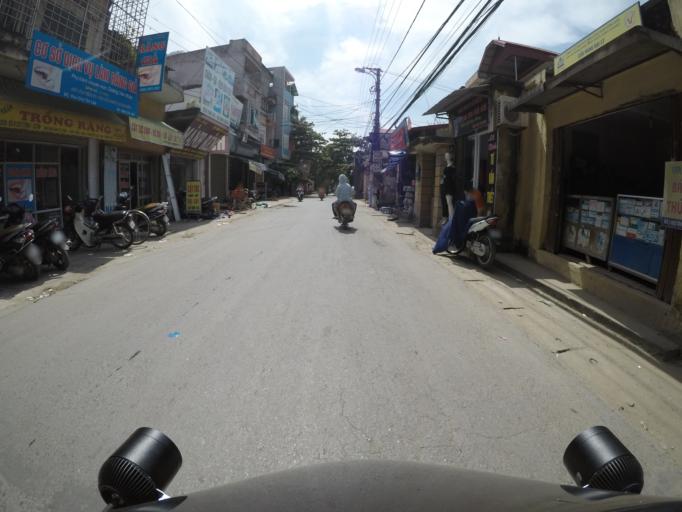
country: VN
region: Ha Noi
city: Troi
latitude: 21.0804
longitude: 105.7099
